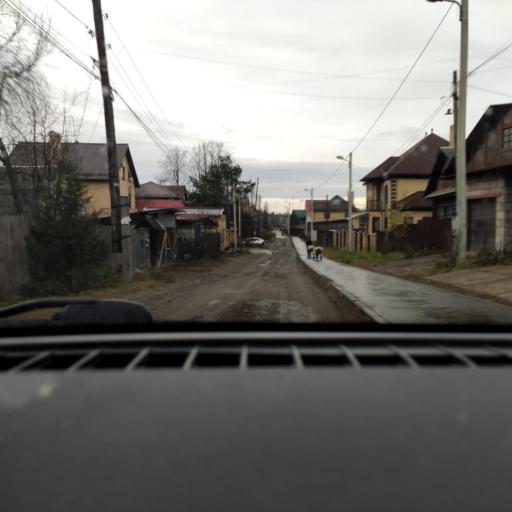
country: RU
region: Perm
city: Kondratovo
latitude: 58.0400
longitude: 56.1179
